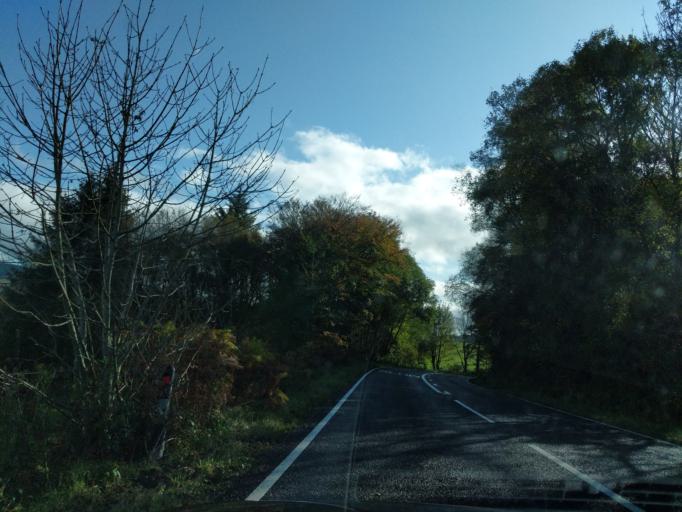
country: GB
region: Scotland
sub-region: Dumfries and Galloway
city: Moffat
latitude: 55.3421
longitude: -3.4591
